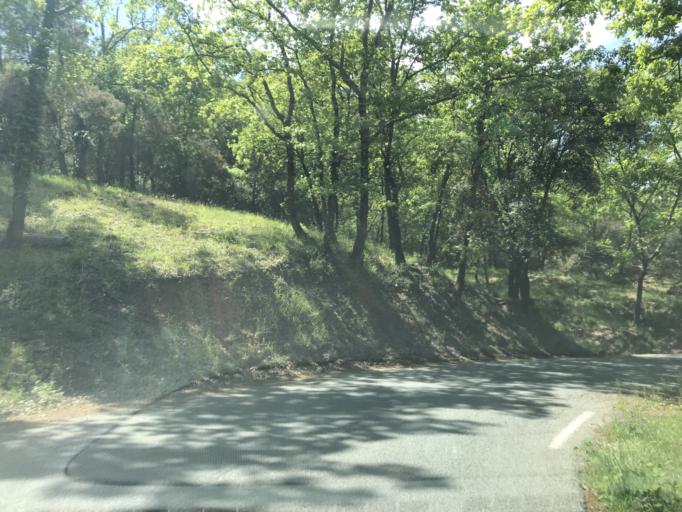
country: FR
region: Provence-Alpes-Cote d'Azur
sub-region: Departement du Var
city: Tanneron
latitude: 43.5851
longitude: 6.8214
